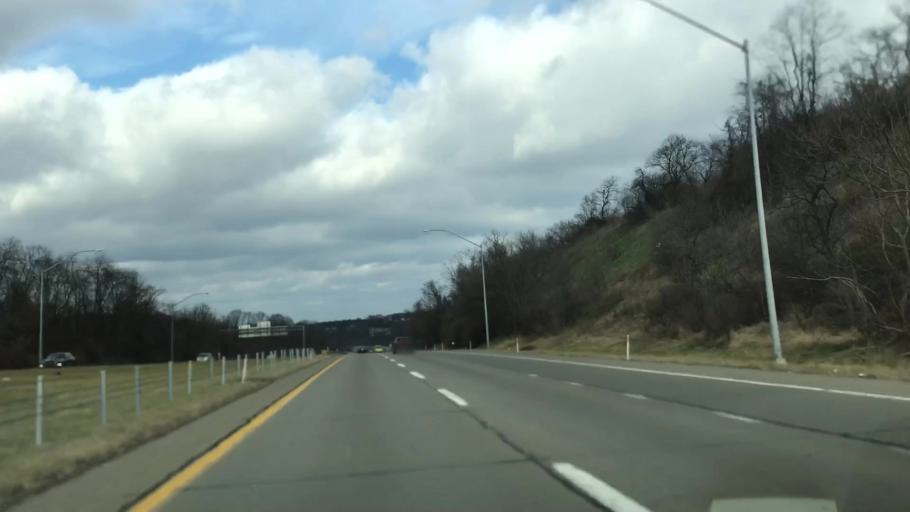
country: US
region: Pennsylvania
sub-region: Allegheny County
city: Ingram
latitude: 40.4550
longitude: -80.1113
